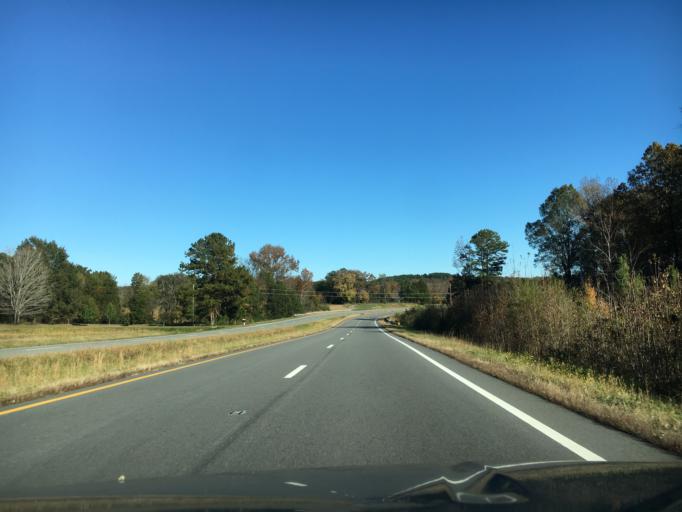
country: US
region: Virginia
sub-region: Mecklenburg County
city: Clarksville
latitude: 36.6613
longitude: -78.7115
